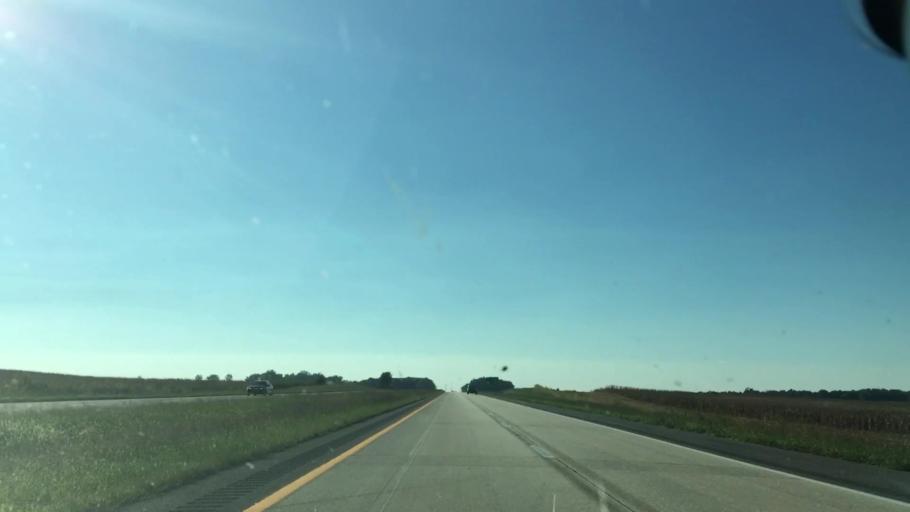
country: US
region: Kentucky
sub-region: Henderson County
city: Henderson
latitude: 37.8027
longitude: -87.5210
